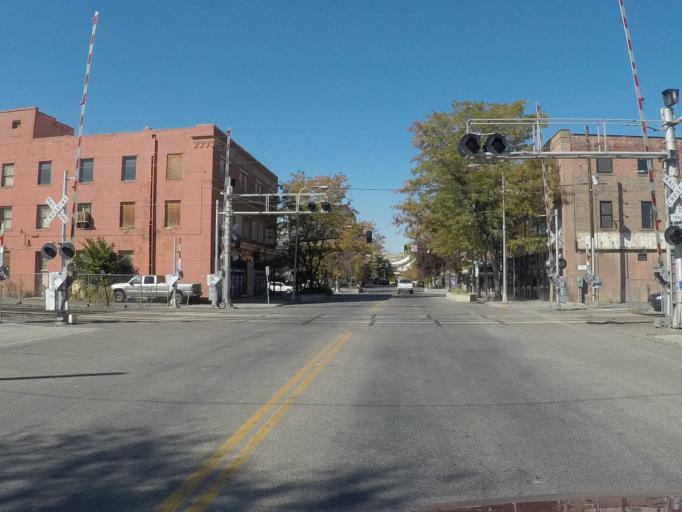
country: US
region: Montana
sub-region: Yellowstone County
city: Billings
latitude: 45.7807
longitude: -108.5044
